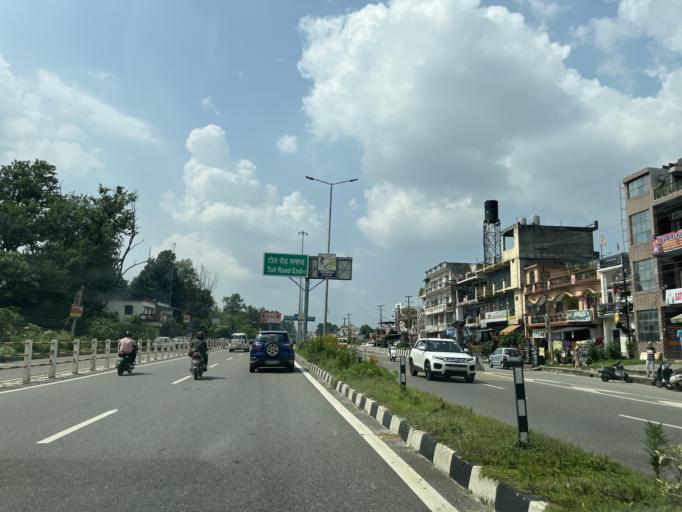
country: IN
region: Uttarakhand
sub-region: Dehradun
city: Raipur
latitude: 30.2720
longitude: 78.0785
